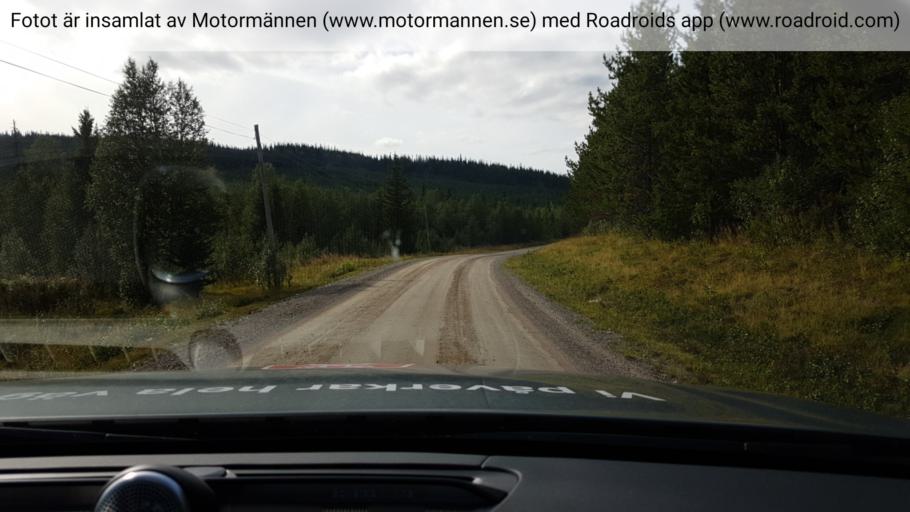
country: SE
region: Jaemtland
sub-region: Stroemsunds Kommun
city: Stroemsund
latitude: 64.5091
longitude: 15.1355
